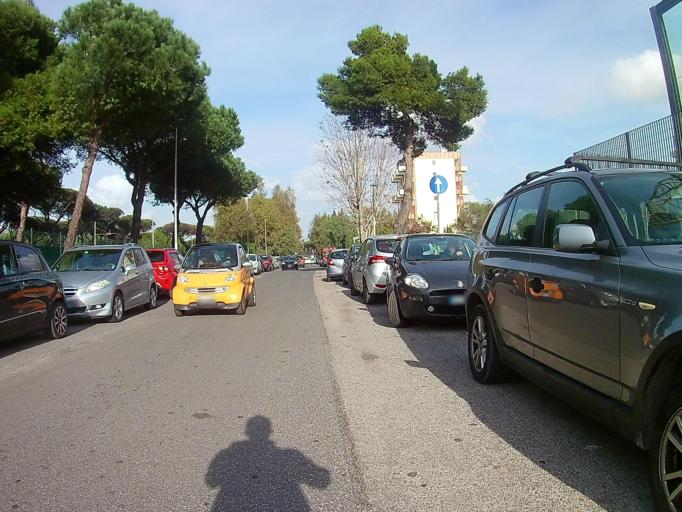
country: IT
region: Latium
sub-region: Citta metropolitana di Roma Capitale
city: Lido di Ostia
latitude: 41.7419
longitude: 12.2858
